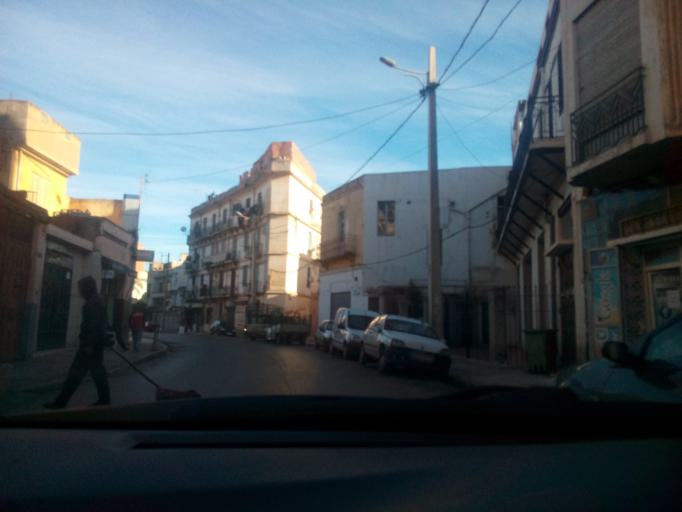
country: DZ
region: Oran
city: Oran
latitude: 35.6895
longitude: -0.6550
